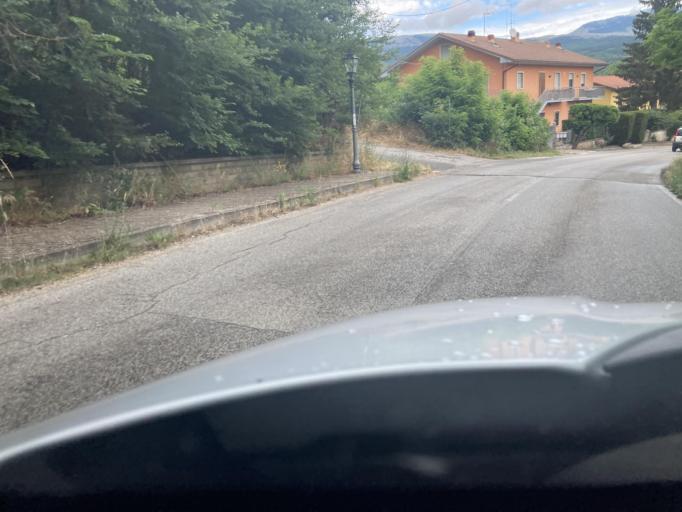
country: IT
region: Abruzzo
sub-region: Provincia dell' Aquila
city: Sant'Eusanio Forconese
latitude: 42.2918
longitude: 13.5269
